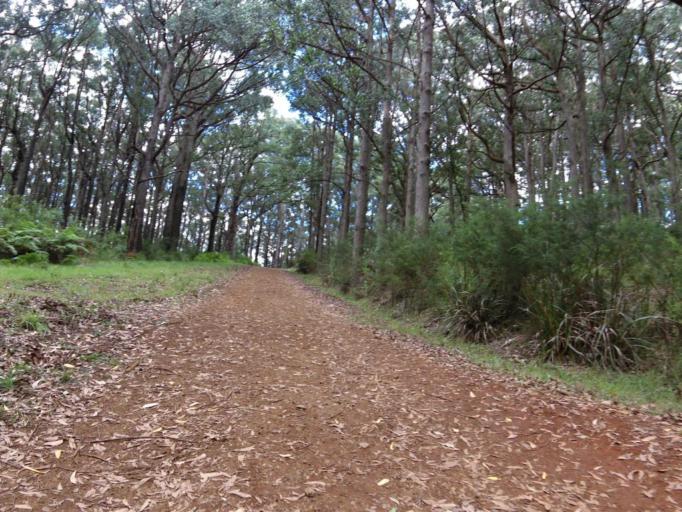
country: AU
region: Victoria
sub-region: Yarra Ranges
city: Olinda
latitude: -37.8570
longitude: 145.3540
